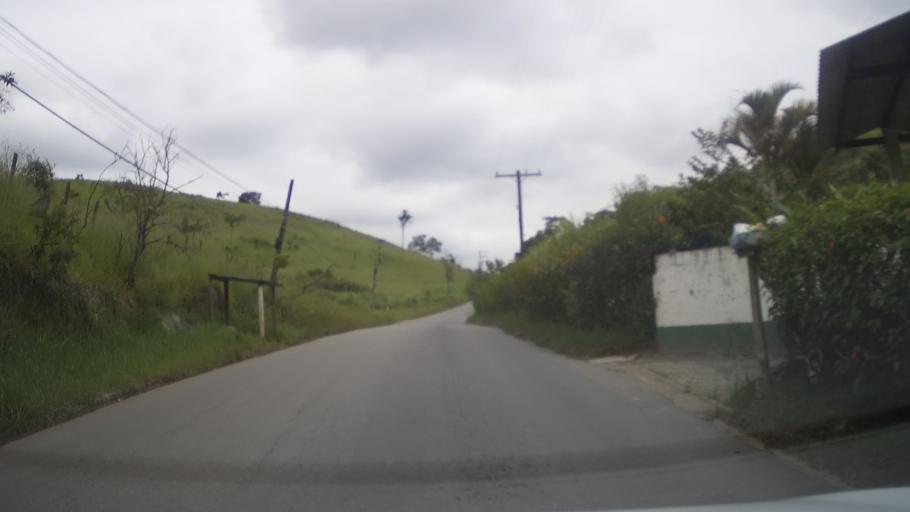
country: BR
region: Sao Paulo
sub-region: Aruja
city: Aruja
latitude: -23.3685
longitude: -46.2936
